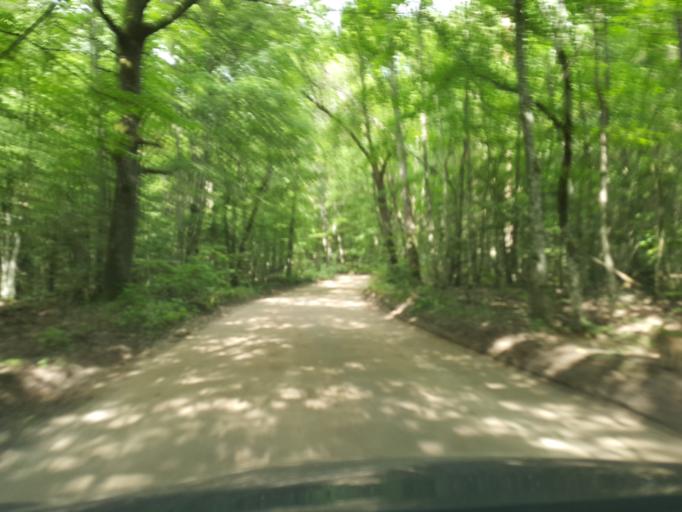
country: LT
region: Alytaus apskritis
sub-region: Alytus
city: Alytus
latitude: 54.3761
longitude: 24.0460
